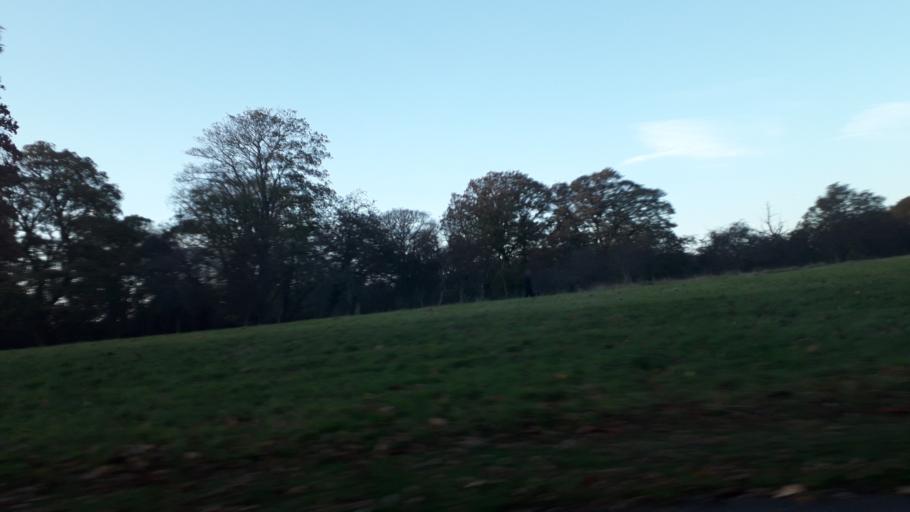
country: IE
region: Leinster
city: Chapelizod
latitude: 53.3602
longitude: -6.3519
